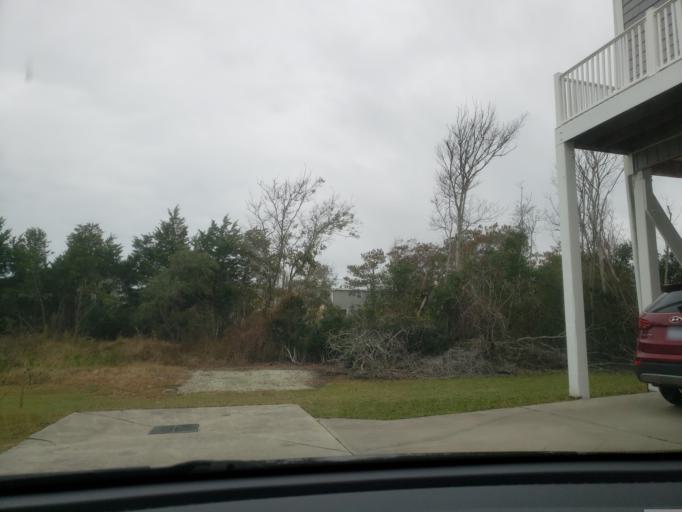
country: US
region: North Carolina
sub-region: Onslow County
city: Sneads Ferry
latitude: 34.5247
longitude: -77.3537
